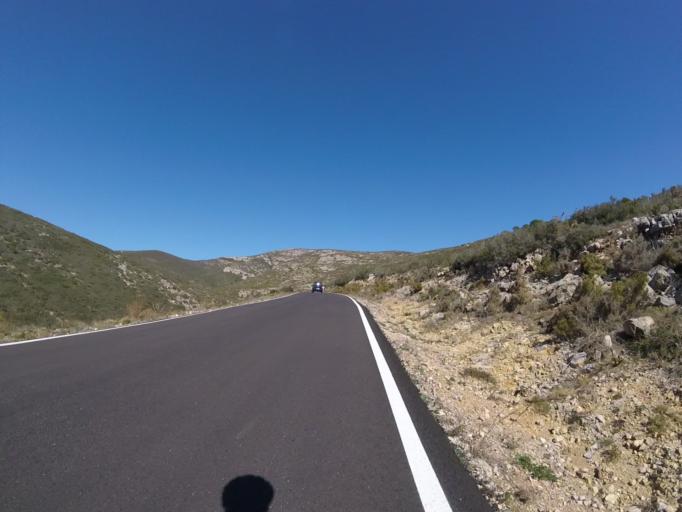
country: ES
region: Valencia
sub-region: Provincia de Castello
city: Cervera del Maestre
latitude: 40.4050
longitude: 0.2274
